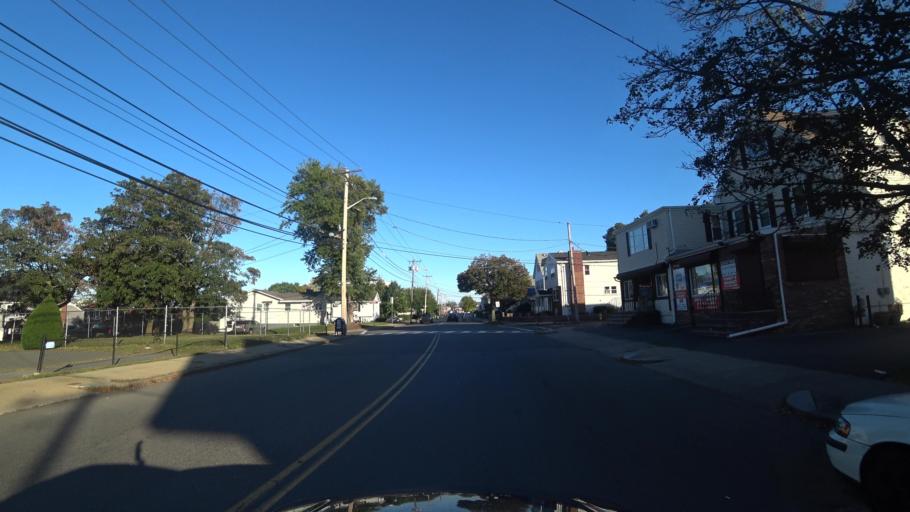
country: US
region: Massachusetts
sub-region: Suffolk County
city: Revere
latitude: 42.4210
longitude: -71.0170
